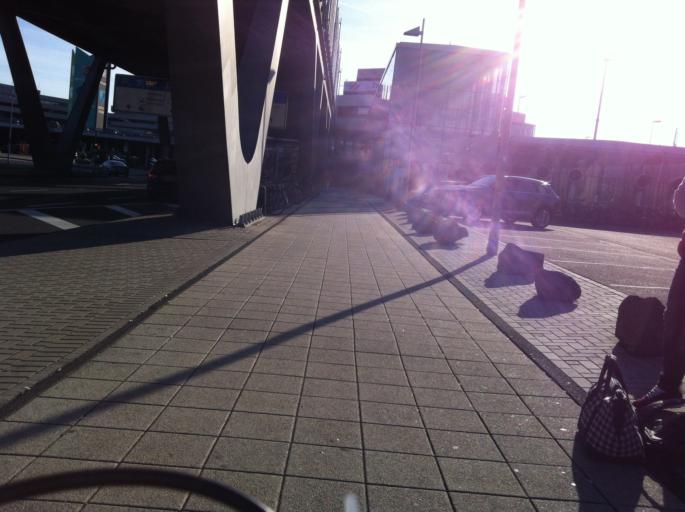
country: DE
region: North Rhine-Westphalia
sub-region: Regierungsbezirk Koln
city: Wahn-Heide
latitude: 50.8778
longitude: 7.1183
